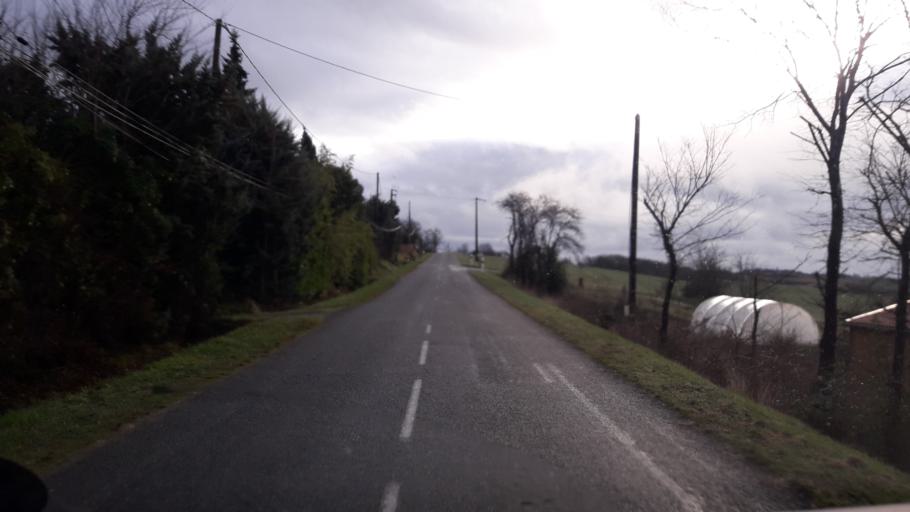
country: FR
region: Midi-Pyrenees
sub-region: Departement de la Haute-Garonne
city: Carbonne
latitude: 43.2607
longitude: 1.2578
